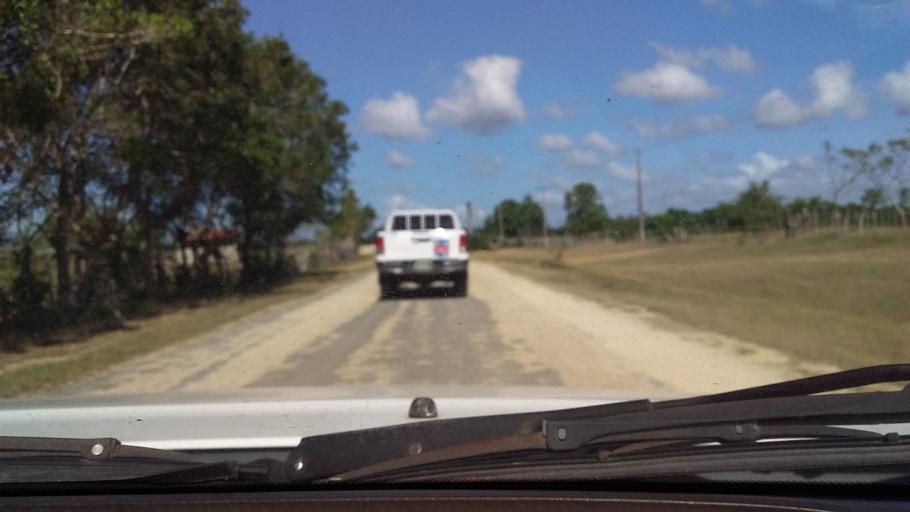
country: DO
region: Santo Domingo
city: Guerra
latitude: 18.5667
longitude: -69.7819
